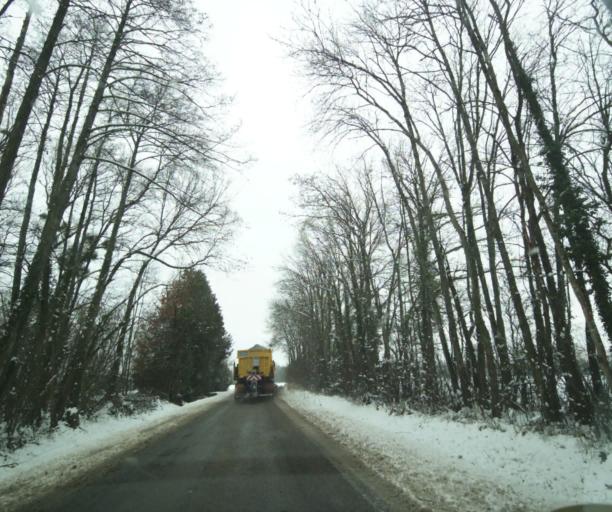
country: FR
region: Champagne-Ardenne
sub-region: Departement de la Haute-Marne
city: Montier-en-Der
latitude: 48.4948
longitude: 4.7110
